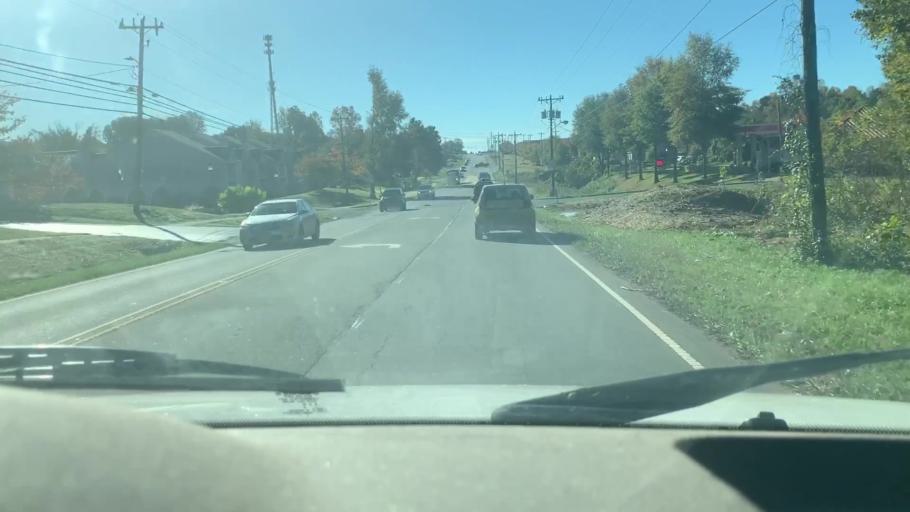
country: US
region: North Carolina
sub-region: Mecklenburg County
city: Huntersville
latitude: 35.4167
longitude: -80.8570
